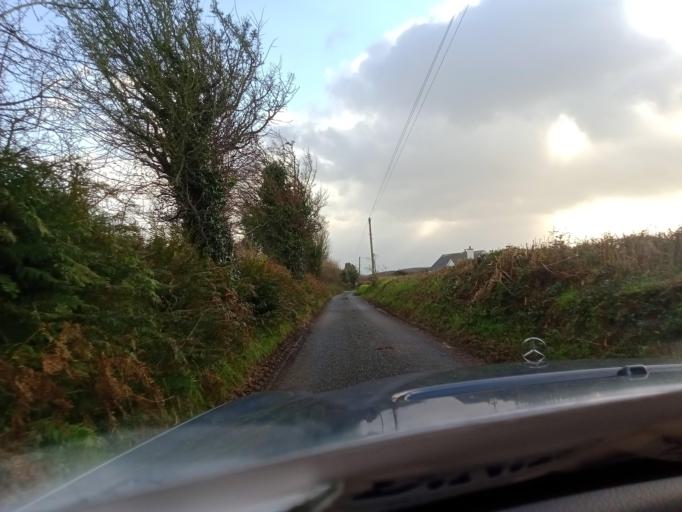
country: IE
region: Leinster
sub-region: Kilkenny
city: Mooncoin
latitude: 52.2841
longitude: -7.2648
